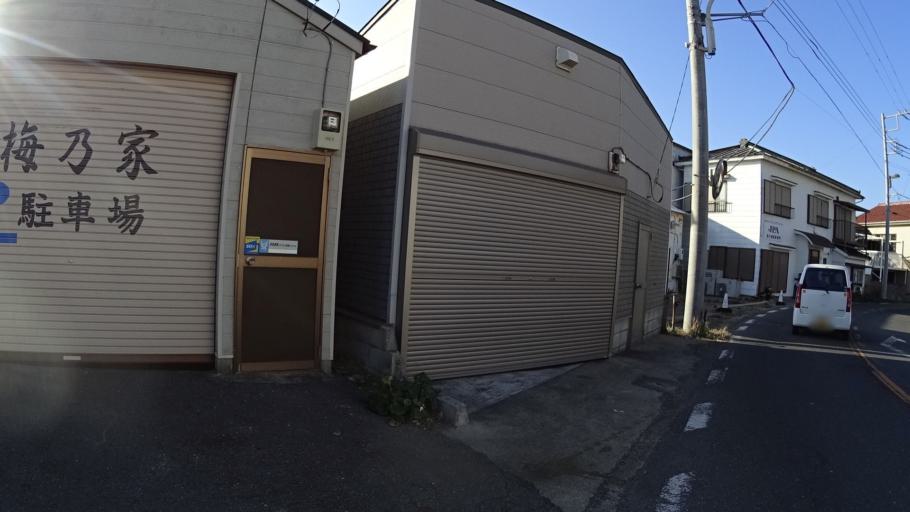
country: JP
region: Kanagawa
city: Miura
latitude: 35.2022
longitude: 139.6049
